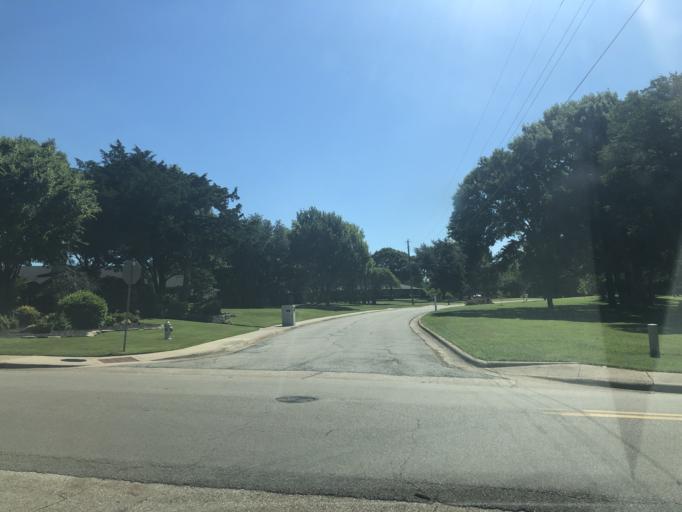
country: US
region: Texas
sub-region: Dallas County
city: Duncanville
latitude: 32.6381
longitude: -96.9354
